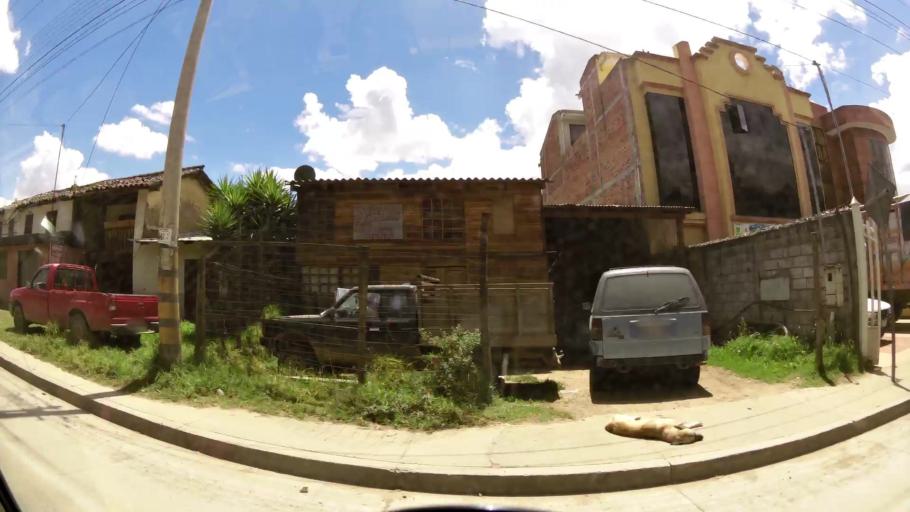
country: EC
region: Azuay
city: Cuenca
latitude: -2.9364
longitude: -79.0458
